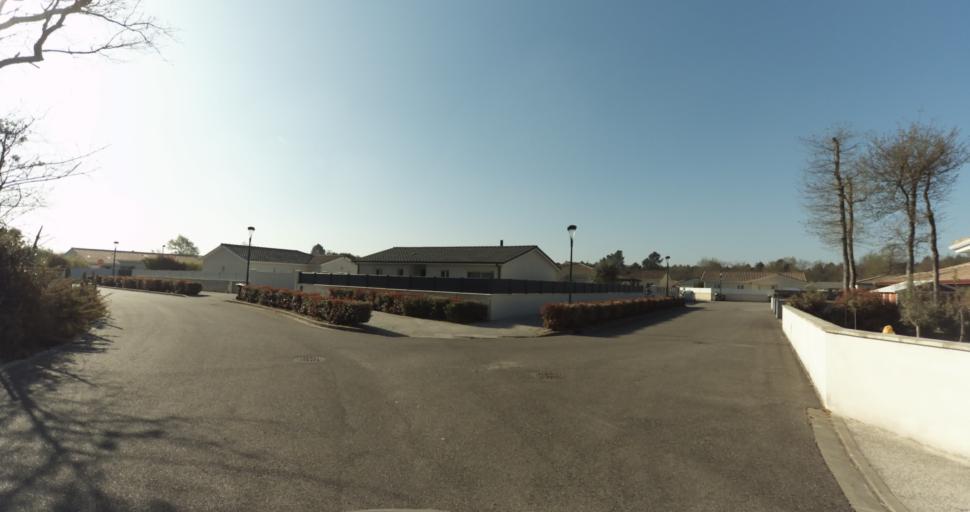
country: FR
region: Aquitaine
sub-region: Departement de la Gironde
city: Martignas-sur-Jalle
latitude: 44.8038
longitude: -0.7961
